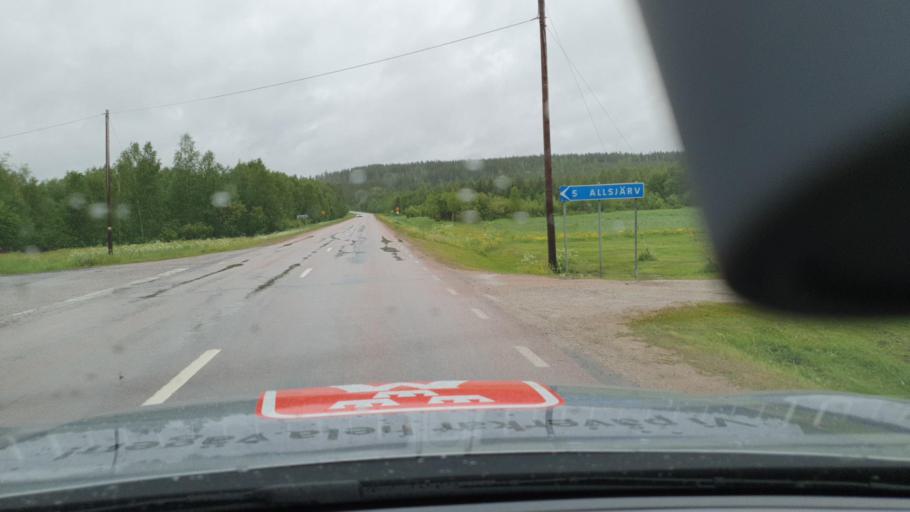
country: SE
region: Norrbotten
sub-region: Overkalix Kommun
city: OEverkalix
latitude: 66.3927
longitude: 22.9420
